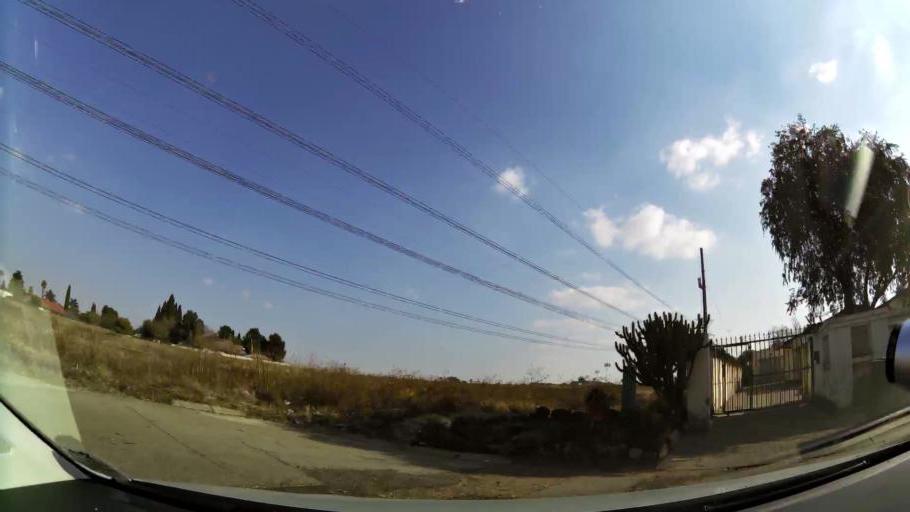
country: ZA
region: Gauteng
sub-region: City of Johannesburg Metropolitan Municipality
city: Modderfontein
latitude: -26.0875
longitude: 28.1982
